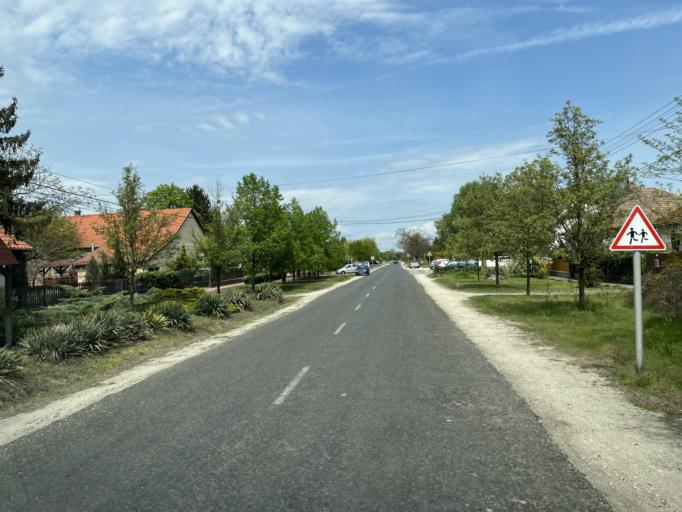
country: HU
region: Pest
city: Csemo
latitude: 47.1148
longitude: 19.6953
